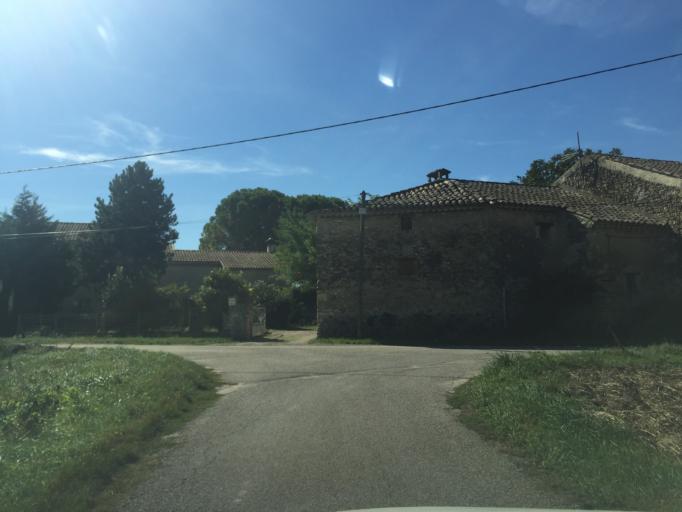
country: FR
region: Provence-Alpes-Cote d'Azur
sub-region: Departement du Vaucluse
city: Caderousse
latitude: 44.1011
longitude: 4.7366
